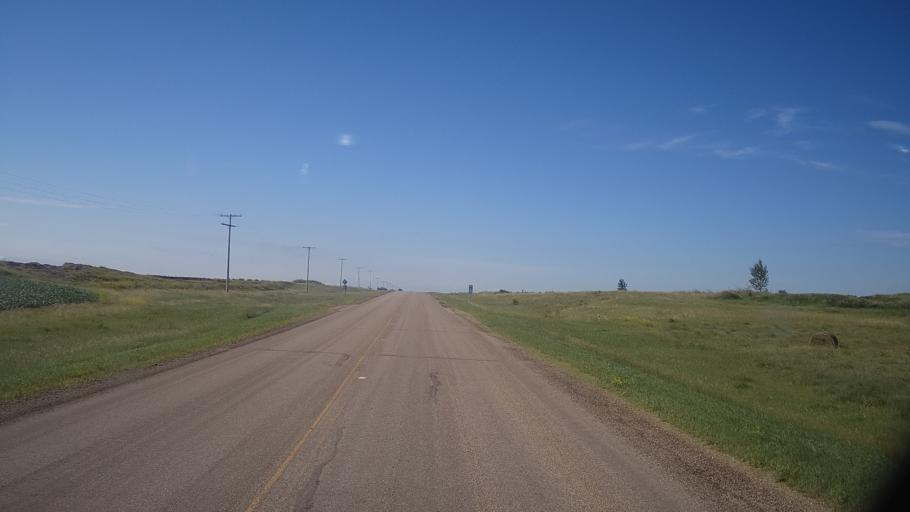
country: CA
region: Saskatchewan
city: Watrous
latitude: 51.7326
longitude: -105.3574
